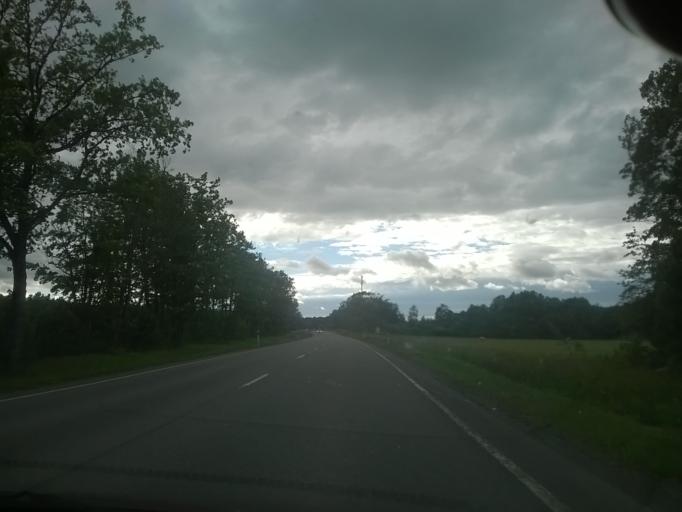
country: EE
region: Laeaene
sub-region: Ridala Parish
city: Uuemoisa
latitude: 58.9593
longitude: 23.7133
